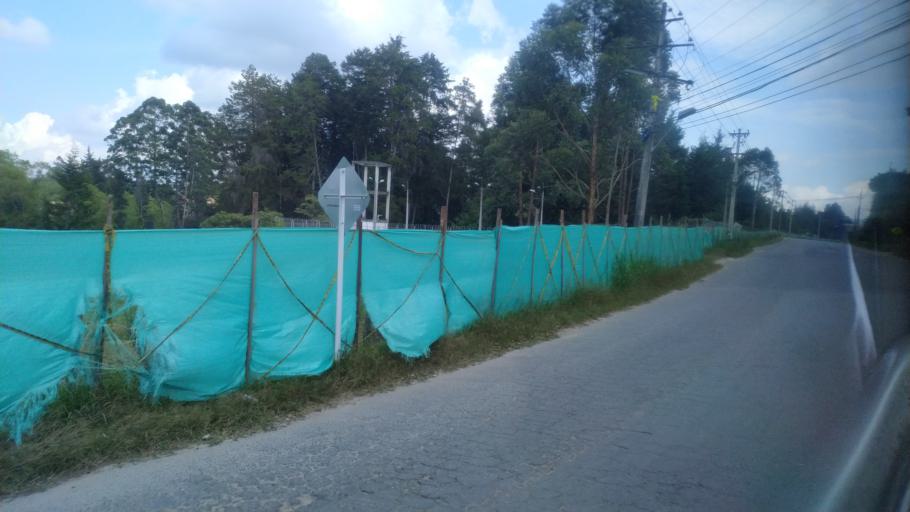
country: CO
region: Antioquia
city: Rionegro
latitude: 6.1712
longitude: -75.3704
